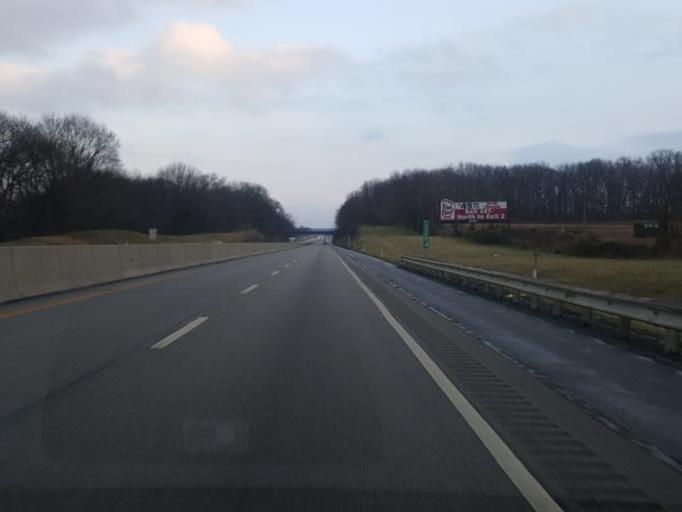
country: US
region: Pennsylvania
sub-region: Cumberland County
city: Schlusser
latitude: 40.2226
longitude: -77.1086
